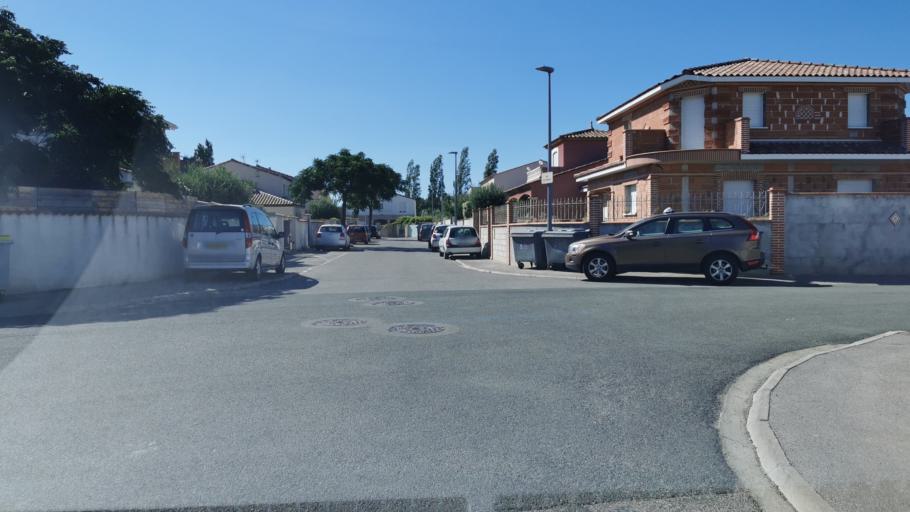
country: FR
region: Languedoc-Roussillon
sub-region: Departement de l'Aude
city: Narbonne
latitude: 43.1989
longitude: 3.0206
